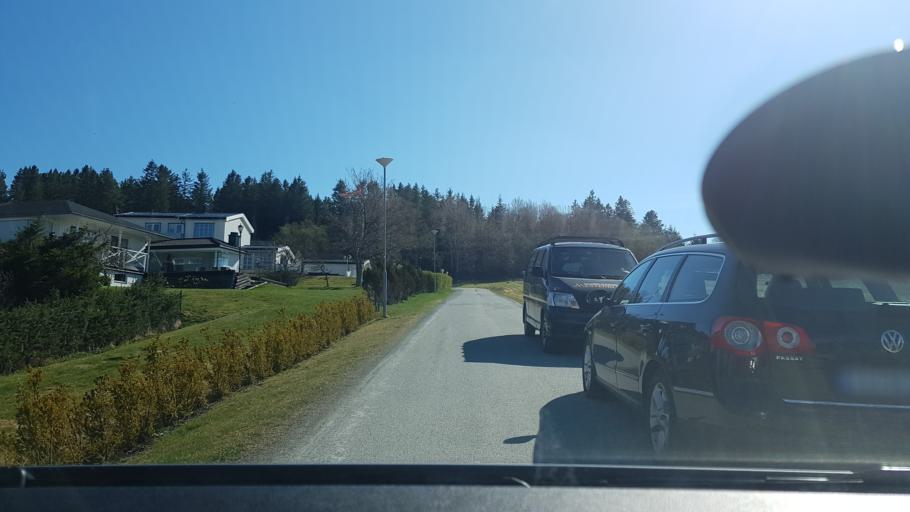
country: NO
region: Sor-Trondelag
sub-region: Trondheim
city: Trondheim
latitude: 63.4169
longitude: 10.4674
